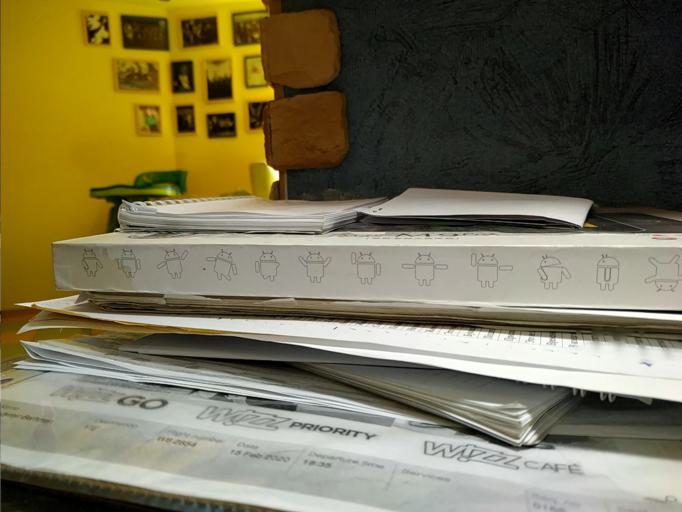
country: RU
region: Novgorod
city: Utorgosh
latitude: 58.2121
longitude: 29.9547
